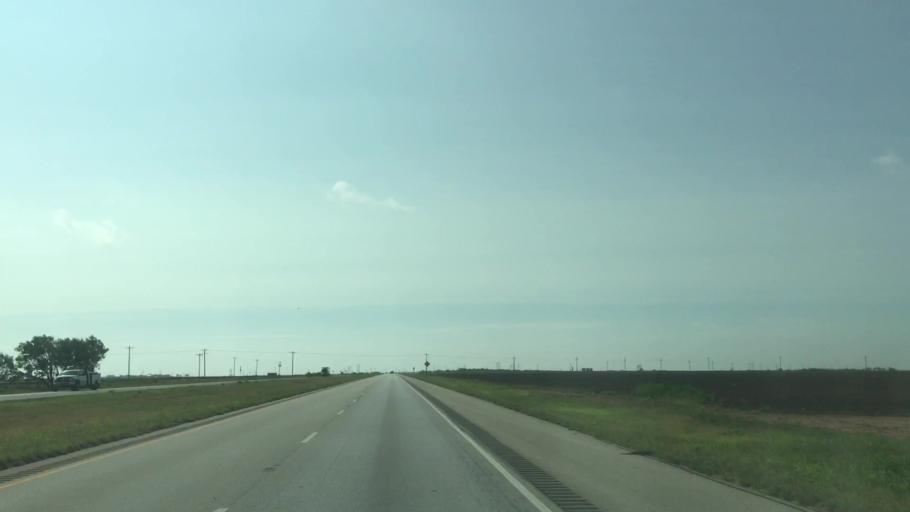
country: US
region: Texas
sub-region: Scurry County
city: Snyder
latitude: 32.6619
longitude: -100.7892
